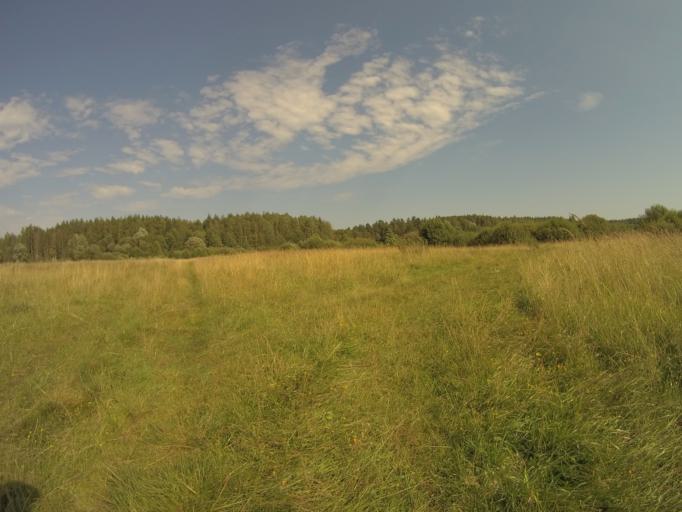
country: RU
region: Vladimir
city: Orgtrud
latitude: 56.0434
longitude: 40.6918
